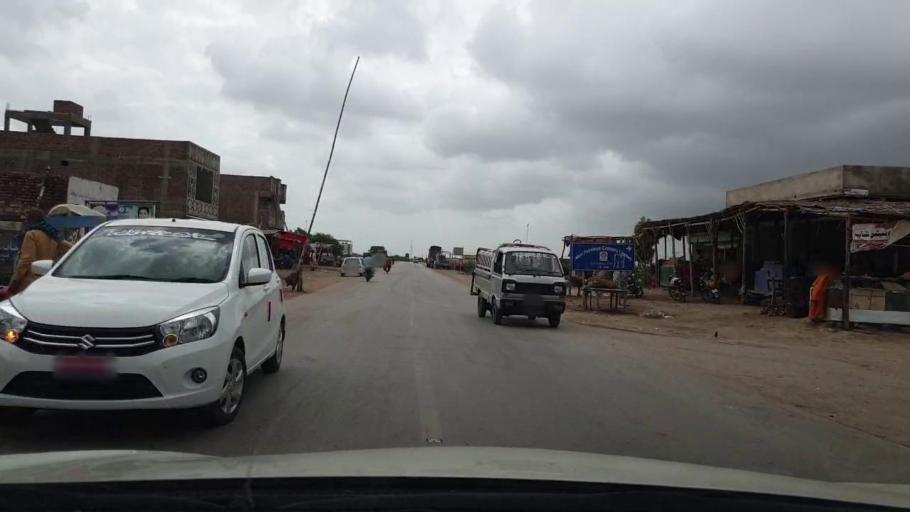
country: PK
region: Sindh
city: Mirpur Batoro
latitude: 24.6439
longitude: 68.4123
